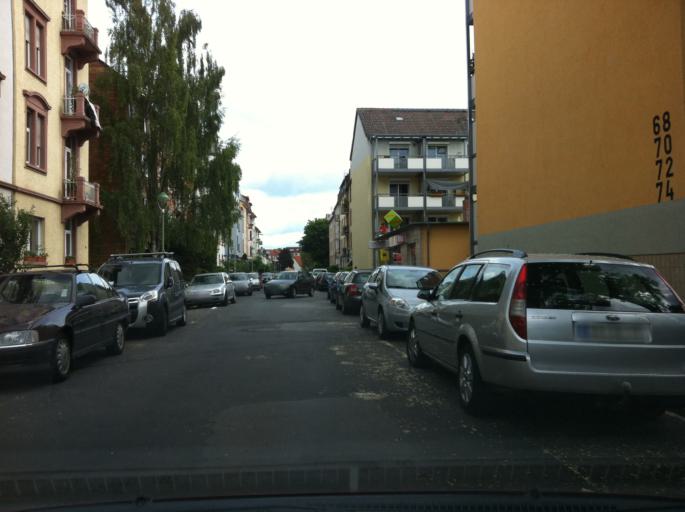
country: DE
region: Hesse
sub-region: Regierungsbezirk Darmstadt
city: Eschborn
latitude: 50.1296
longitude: 8.6143
